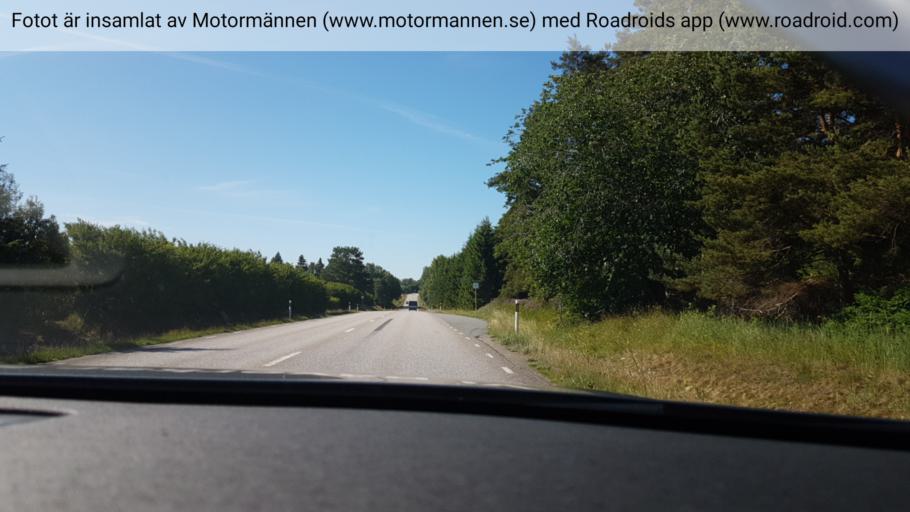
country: SE
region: Vaestra Goetaland
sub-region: Ulricehamns Kommun
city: Ulricehamn
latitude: 57.8688
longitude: 13.4311
